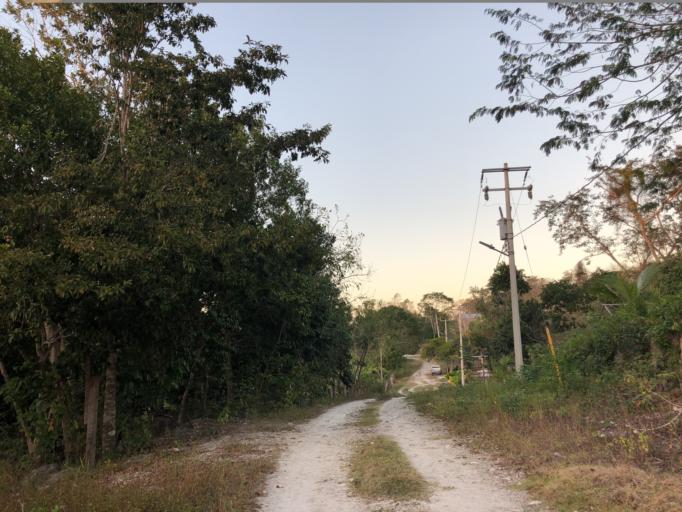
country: MX
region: Quintana Roo
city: Nicolas Bravo
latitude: 18.4526
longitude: -89.3049
